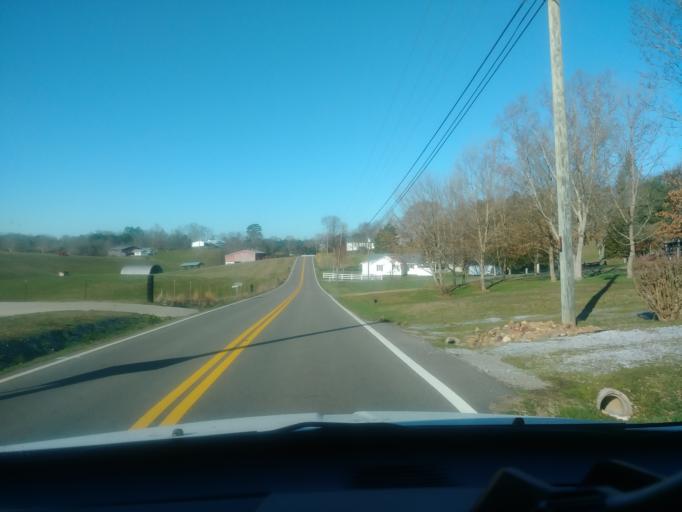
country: US
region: Tennessee
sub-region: Greene County
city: Mosheim
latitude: 36.1159
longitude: -82.9604
